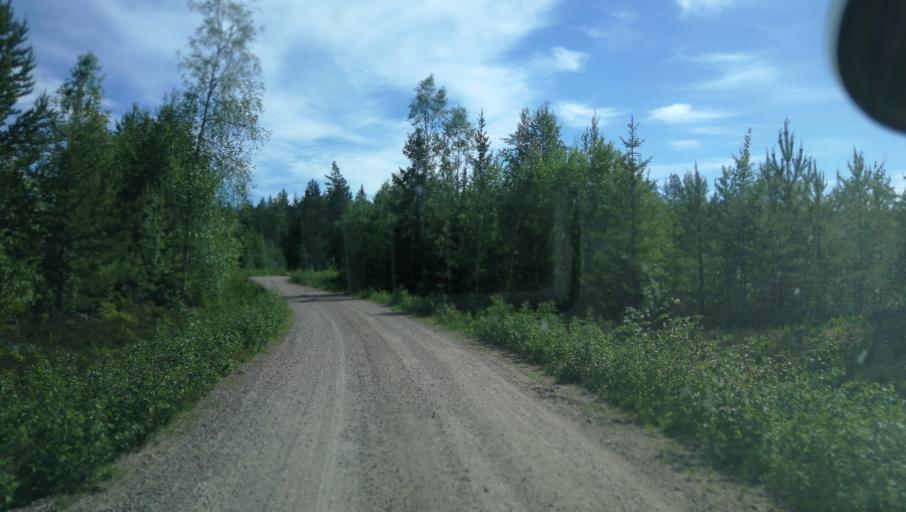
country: SE
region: Dalarna
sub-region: Vansbro Kommun
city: Vansbro
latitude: 60.8337
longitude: 14.1582
